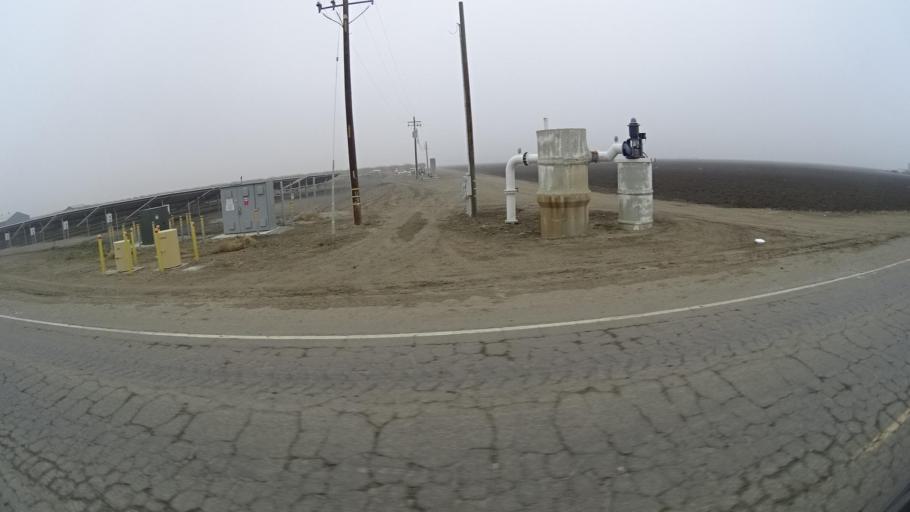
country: US
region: California
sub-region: Kern County
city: Buttonwillow
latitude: 35.4355
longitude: -119.5182
